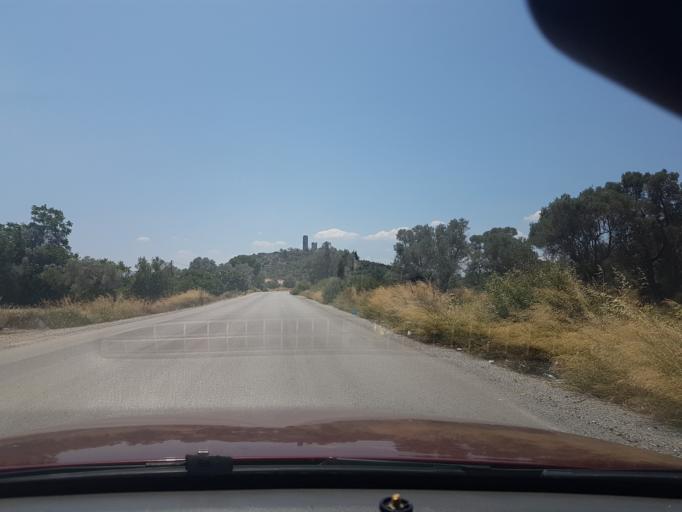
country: GR
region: Central Greece
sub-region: Nomos Evvoias
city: Filla
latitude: 38.4499
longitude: 23.6754
